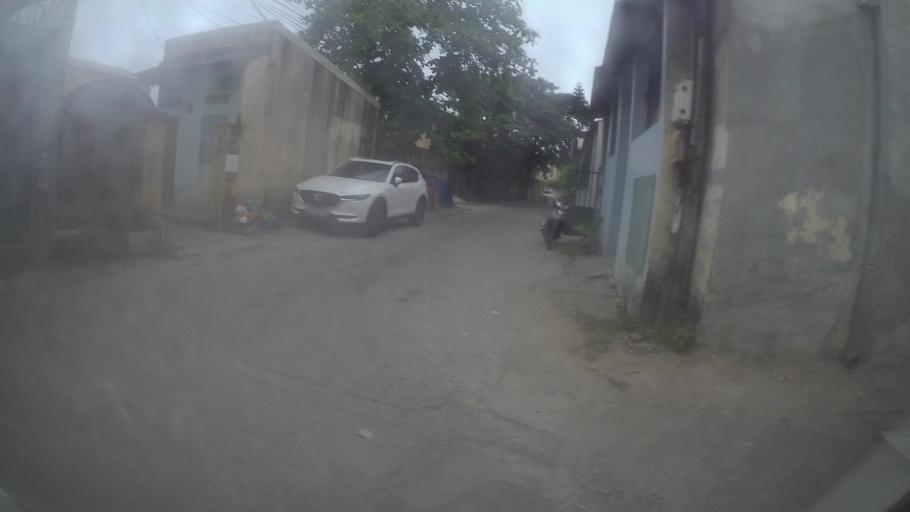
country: VN
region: Da Nang
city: Son Tra
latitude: 16.0450
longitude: 108.2450
